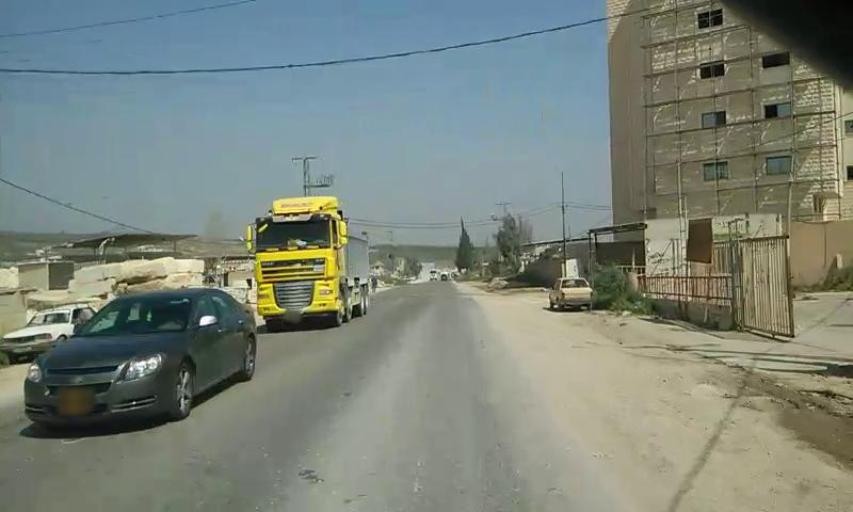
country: PS
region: West Bank
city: Ash Shuhada'
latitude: 32.4347
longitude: 35.2708
